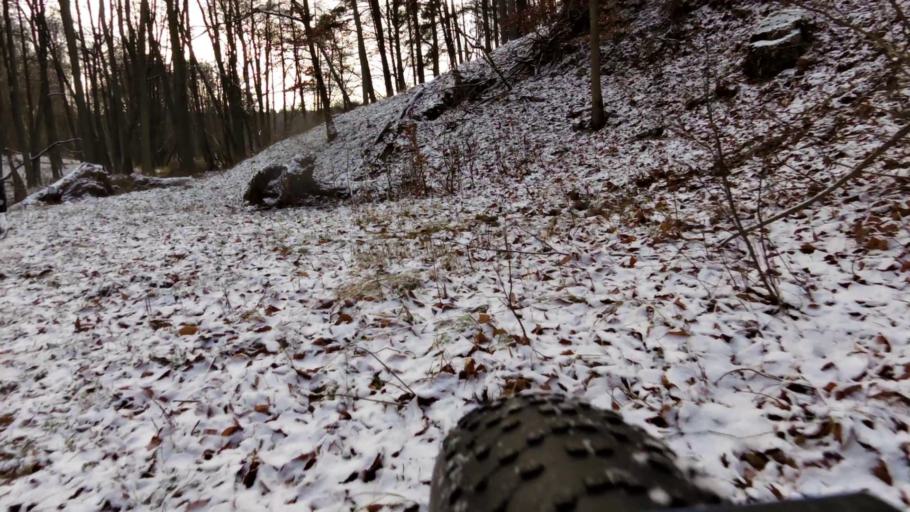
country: PL
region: West Pomeranian Voivodeship
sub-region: Powiat walecki
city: Tuczno
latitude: 53.2991
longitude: 16.2886
